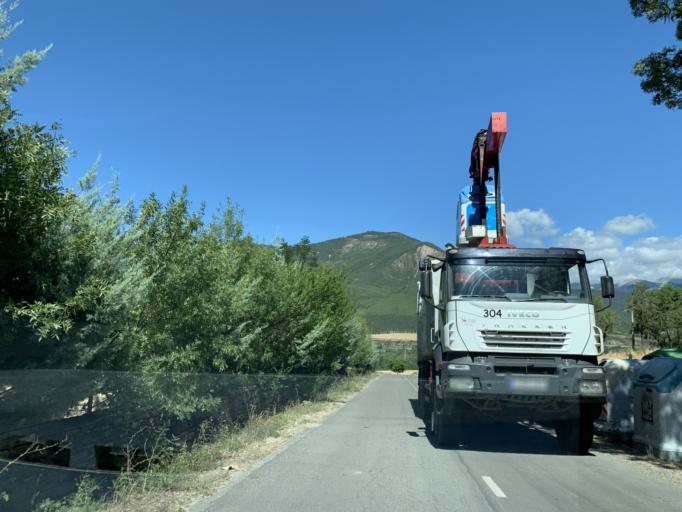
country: ES
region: Aragon
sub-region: Provincia de Huesca
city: Sabinanigo
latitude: 42.5513
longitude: -0.3168
